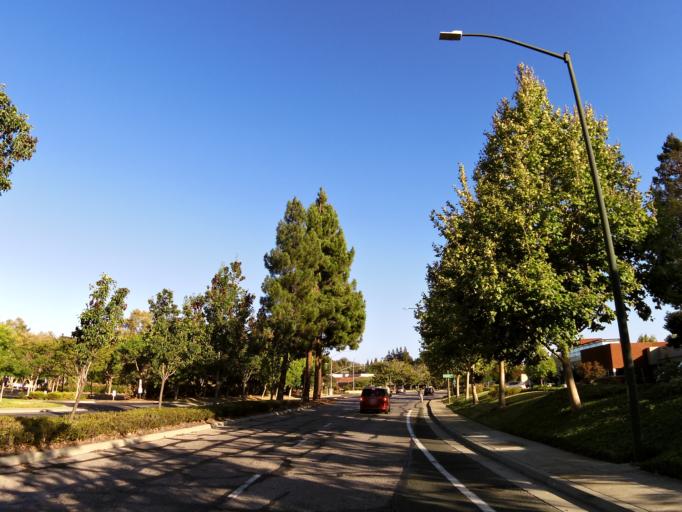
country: US
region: California
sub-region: Santa Clara County
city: Sunnyvale
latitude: 37.3915
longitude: -122.0490
